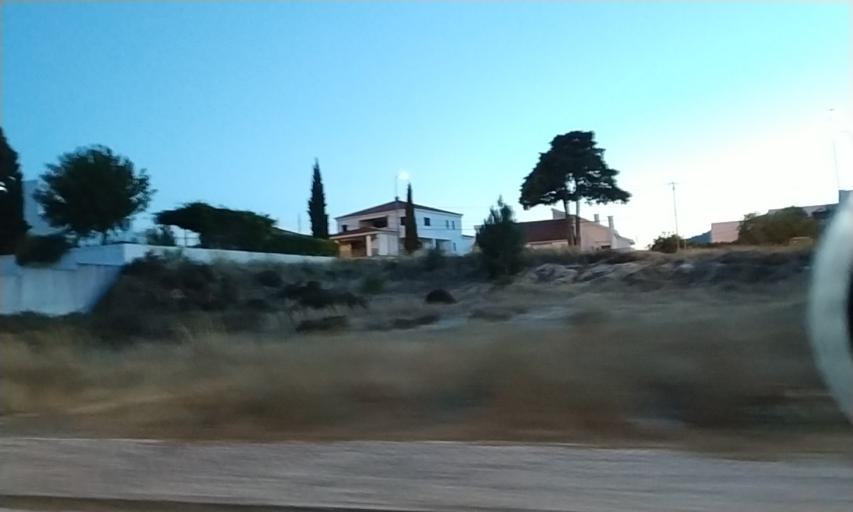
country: PT
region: Setubal
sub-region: Palmela
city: Palmela
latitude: 38.5462
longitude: -8.8976
